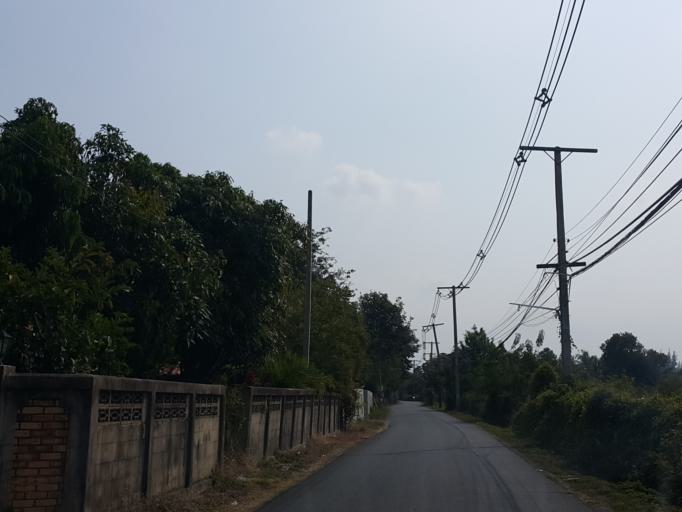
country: TH
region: Chiang Mai
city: San Kamphaeng
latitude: 18.8099
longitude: 99.1231
